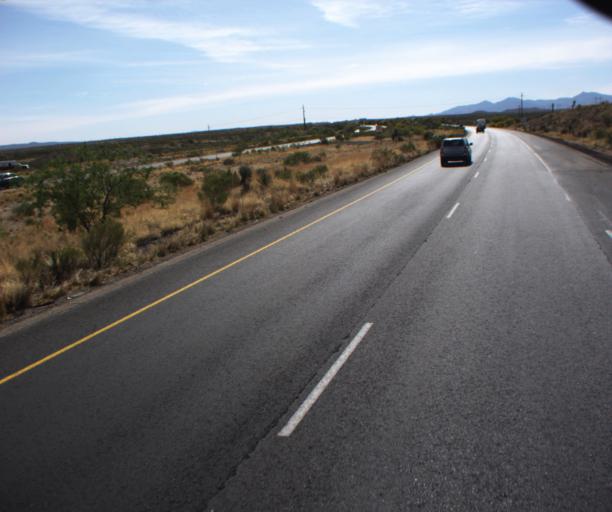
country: US
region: Arizona
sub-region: Pima County
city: Vail
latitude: 32.0038
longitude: -110.6857
